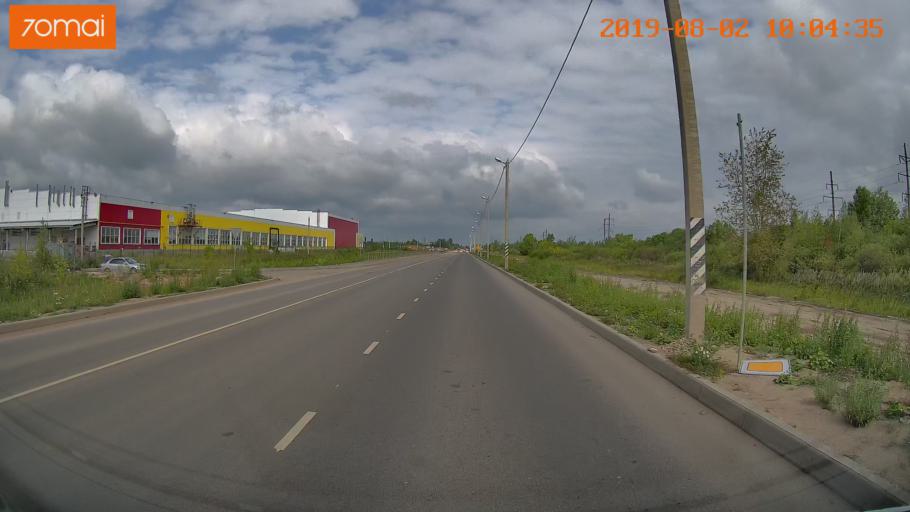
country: RU
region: Ivanovo
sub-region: Gorod Ivanovo
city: Ivanovo
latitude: 56.9736
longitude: 40.9245
